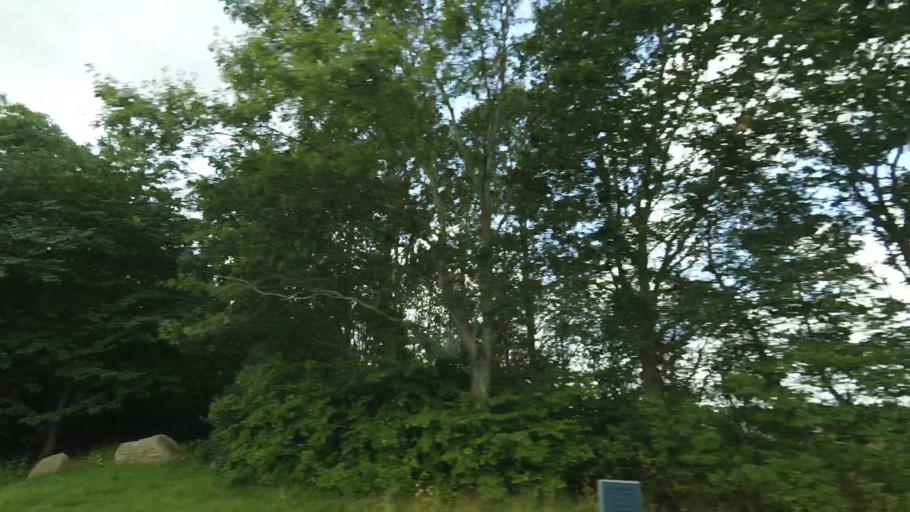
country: DK
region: Central Jutland
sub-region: Norddjurs Kommune
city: Auning
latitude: 56.4982
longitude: 10.4362
